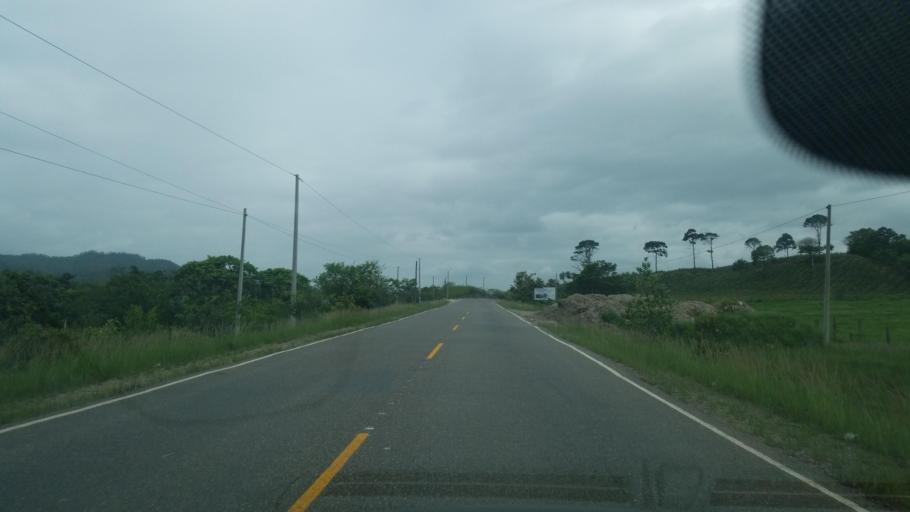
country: HN
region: Ocotepeque
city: Lucerna
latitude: 14.5701
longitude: -88.9307
